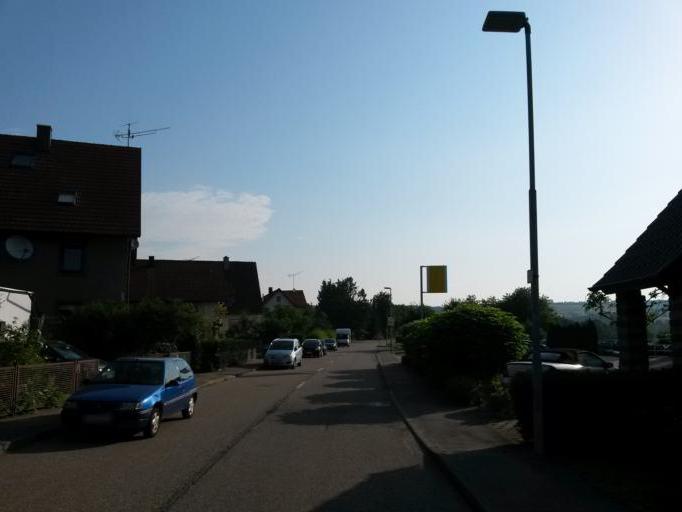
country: DE
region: Baden-Wuerttemberg
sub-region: Karlsruhe Region
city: Neuenburg
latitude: 48.8913
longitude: 8.5700
